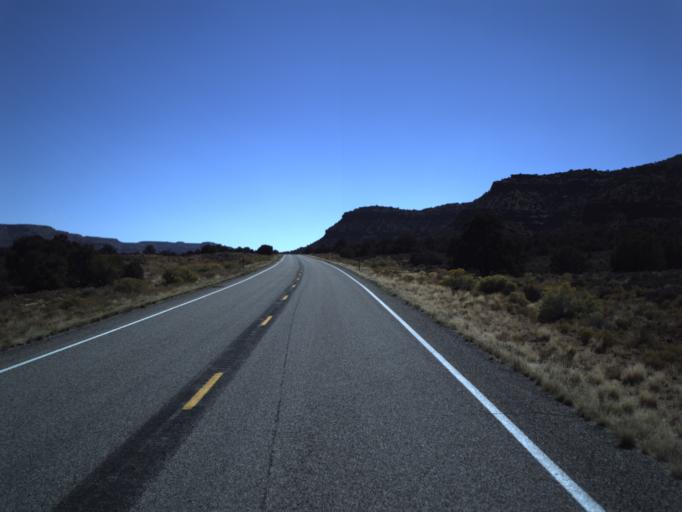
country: US
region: Utah
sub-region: San Juan County
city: Blanding
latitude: 37.6671
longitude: -110.1964
